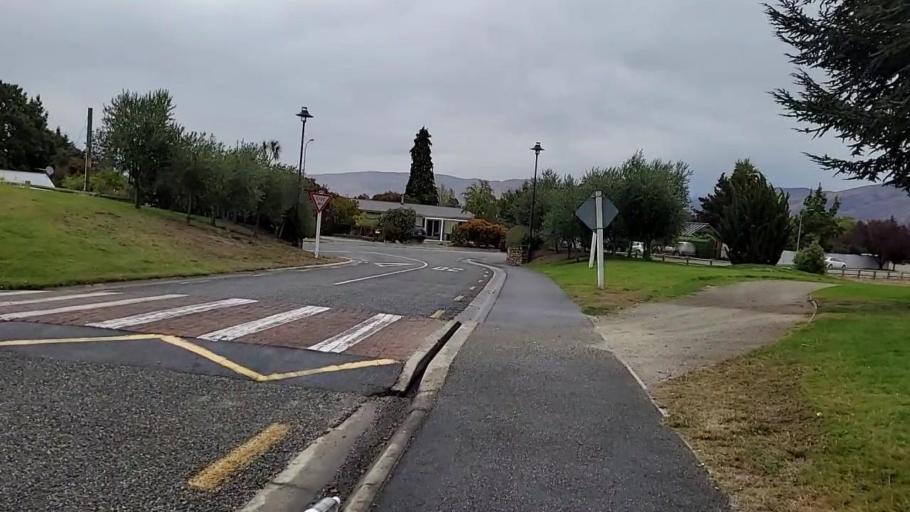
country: NZ
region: Otago
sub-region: Queenstown-Lakes District
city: Wanaka
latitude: -45.0408
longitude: 169.2077
